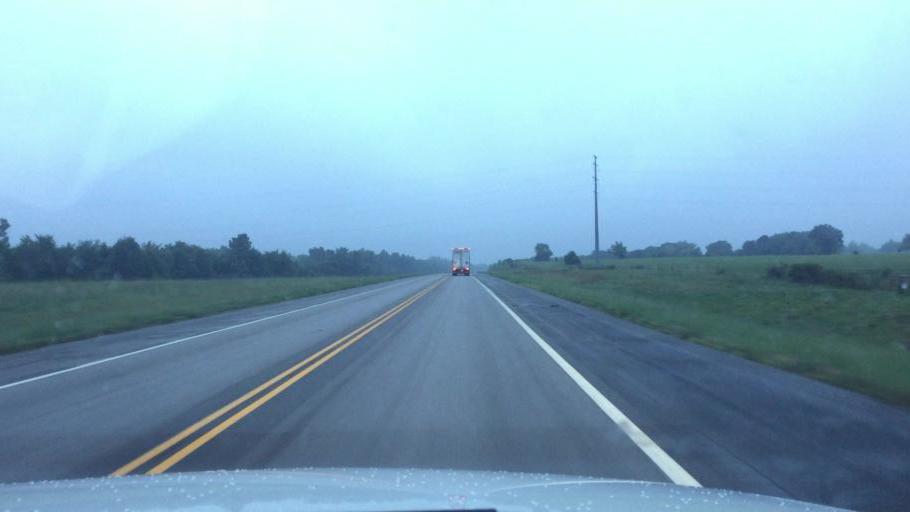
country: US
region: Kansas
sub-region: Montgomery County
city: Cherryvale
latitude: 37.4530
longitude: -95.4829
